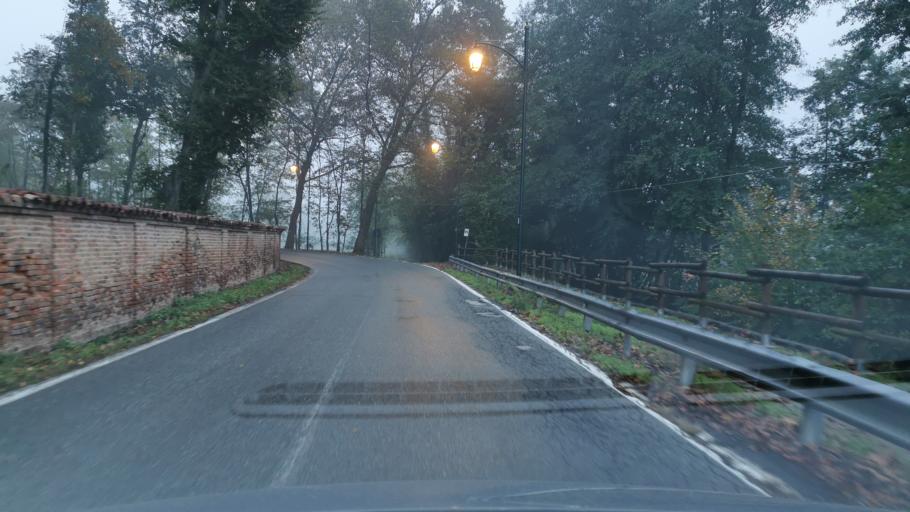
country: IT
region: Piedmont
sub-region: Provincia di Torino
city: Aglie
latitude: 45.3597
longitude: 7.7694
